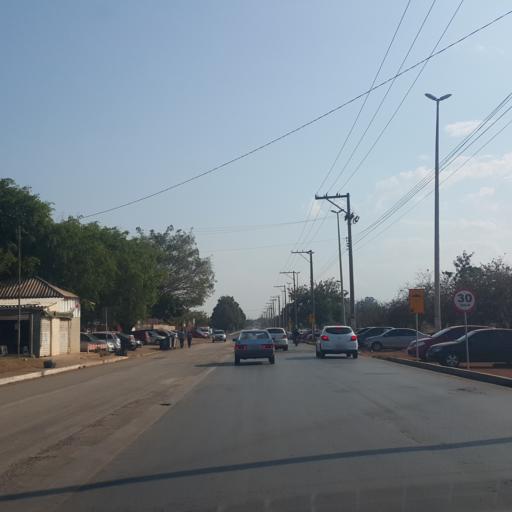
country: BR
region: Federal District
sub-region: Brasilia
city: Brasilia
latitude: -15.8685
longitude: -48.0374
